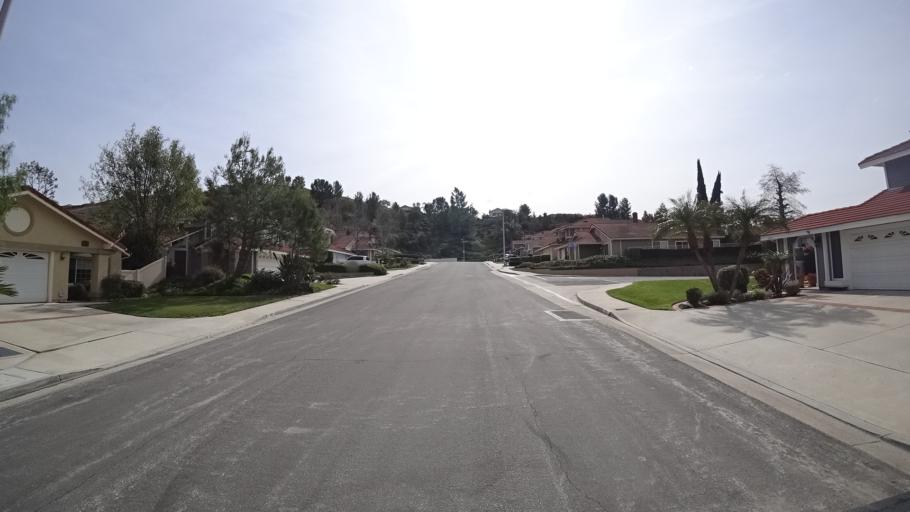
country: US
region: California
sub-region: Orange County
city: Yorba Linda
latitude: 33.8613
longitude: -117.7492
